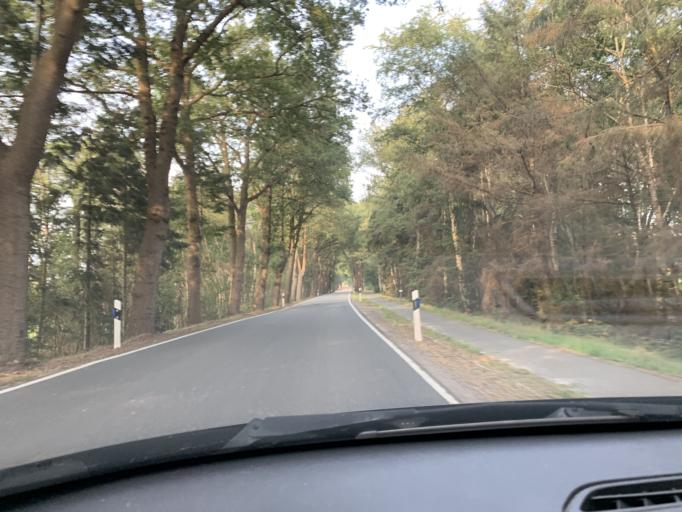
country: DE
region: Lower Saxony
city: Apen
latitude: 53.1951
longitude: 7.7881
